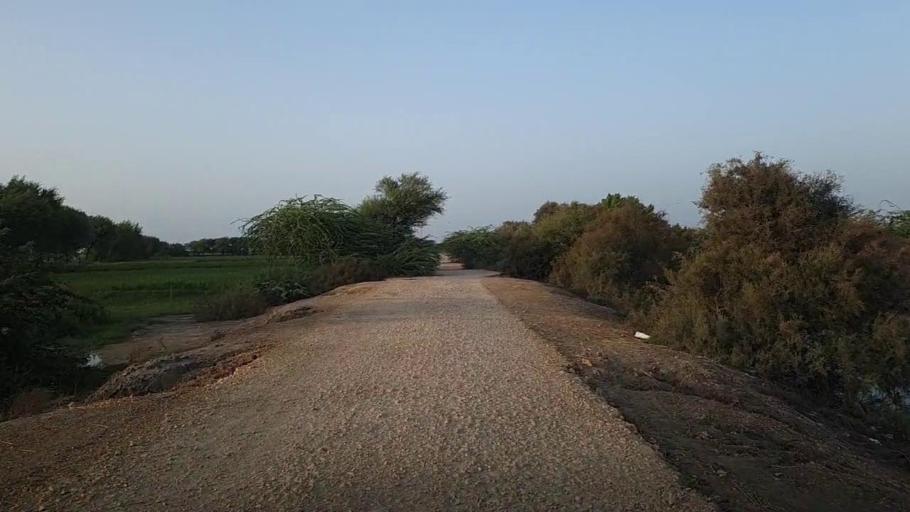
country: PK
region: Sindh
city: Kario
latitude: 24.7185
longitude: 68.4622
